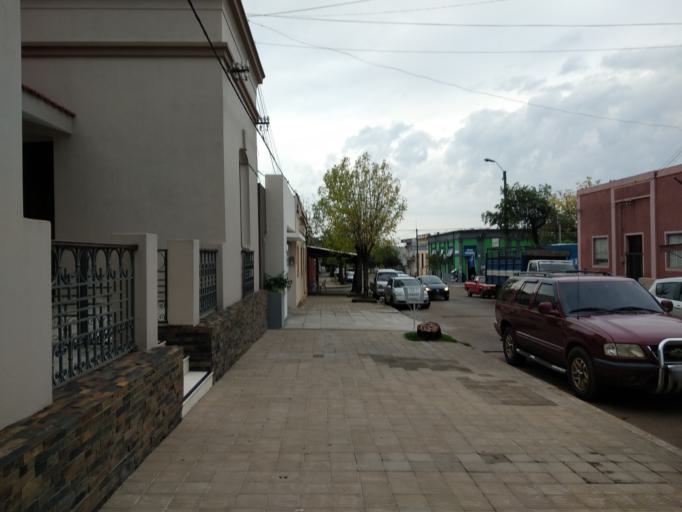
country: UY
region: Artigas
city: Artigas
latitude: -30.4034
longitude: -56.4654
